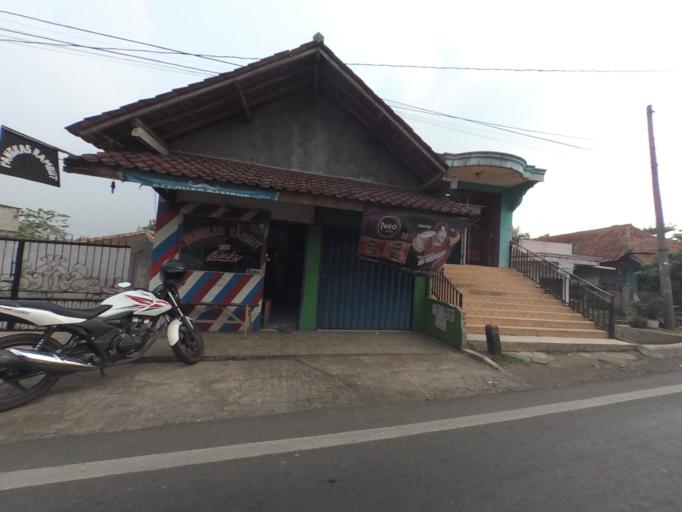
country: ID
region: West Java
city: Ciampea
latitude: -6.5636
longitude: 106.6801
